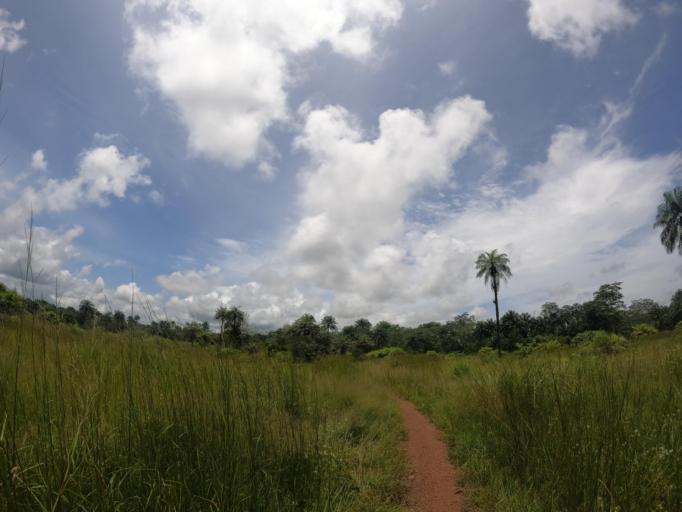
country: SL
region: Northern Province
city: Binkolo
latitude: 9.1479
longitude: -12.2469
